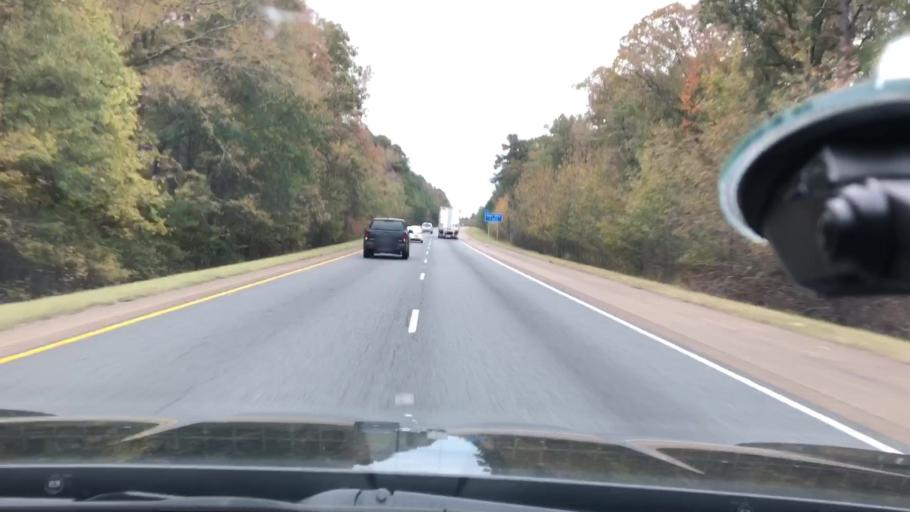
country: US
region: Arkansas
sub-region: Clark County
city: Gurdon
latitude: 33.9175
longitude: -93.2774
